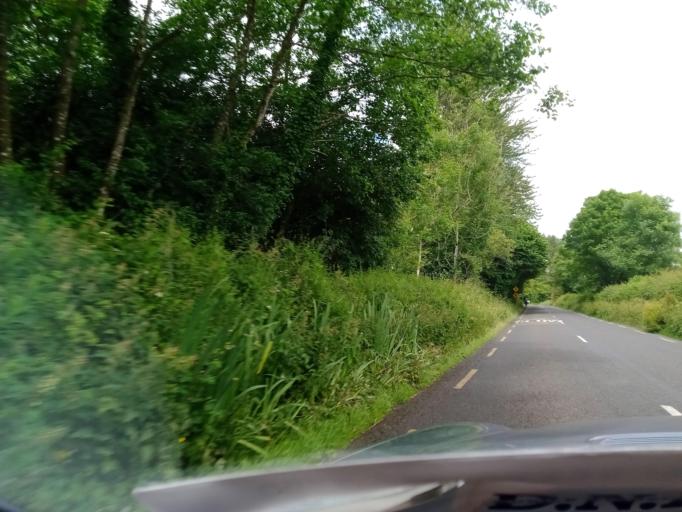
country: IE
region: Leinster
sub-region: Kilkenny
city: Piltown
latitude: 52.4696
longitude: -7.2748
